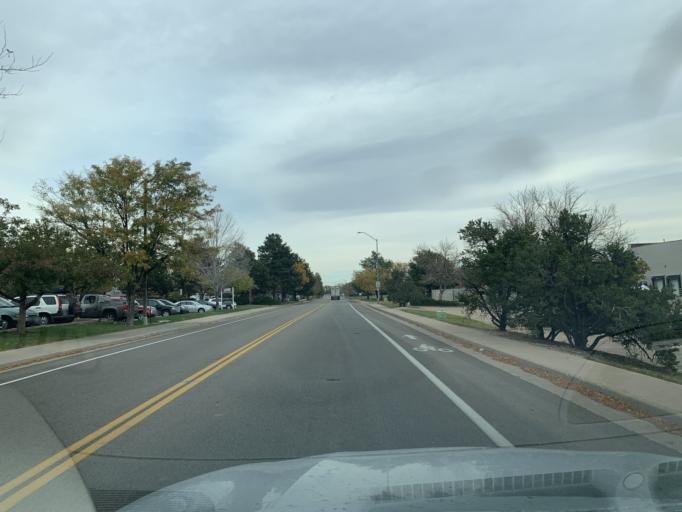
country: US
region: Colorado
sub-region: Larimer County
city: Fort Collins
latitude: 40.5300
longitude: -105.0795
